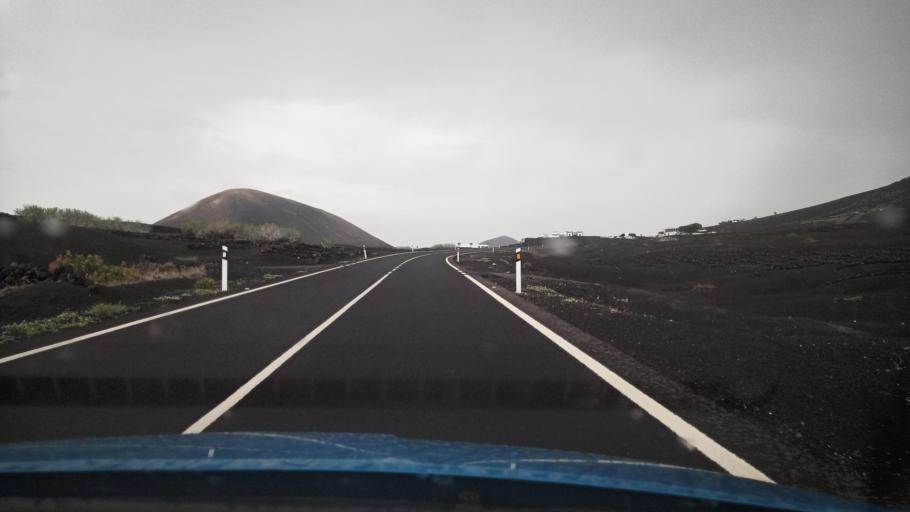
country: ES
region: Canary Islands
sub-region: Provincia de Las Palmas
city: Yaiza
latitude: 28.9659
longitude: -13.7210
